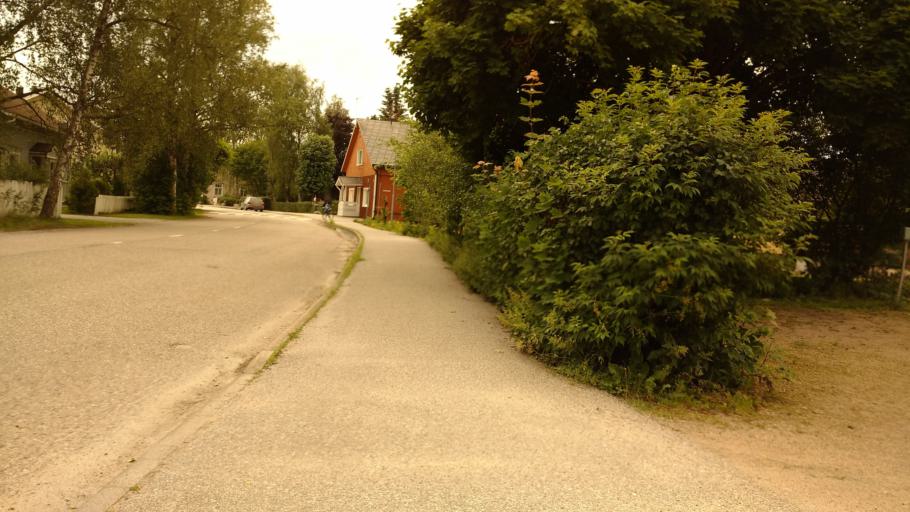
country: FI
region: Varsinais-Suomi
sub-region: Salo
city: Salo
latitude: 60.3925
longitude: 23.1258
